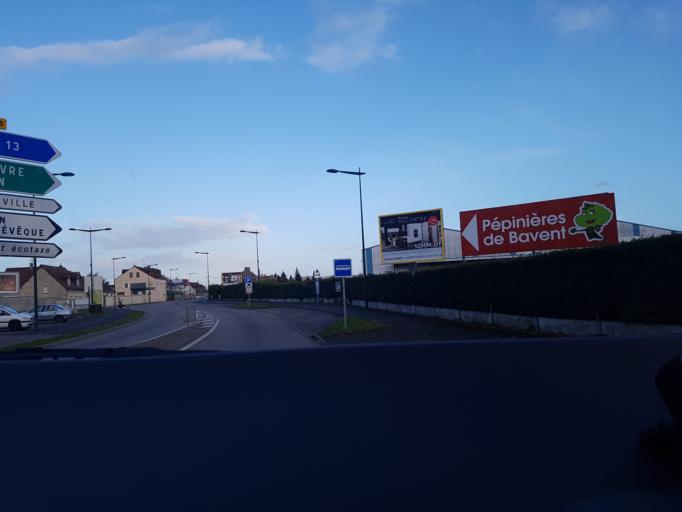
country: FR
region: Lower Normandy
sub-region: Departement du Calvados
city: Giberville
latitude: 49.1722
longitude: -0.2821
